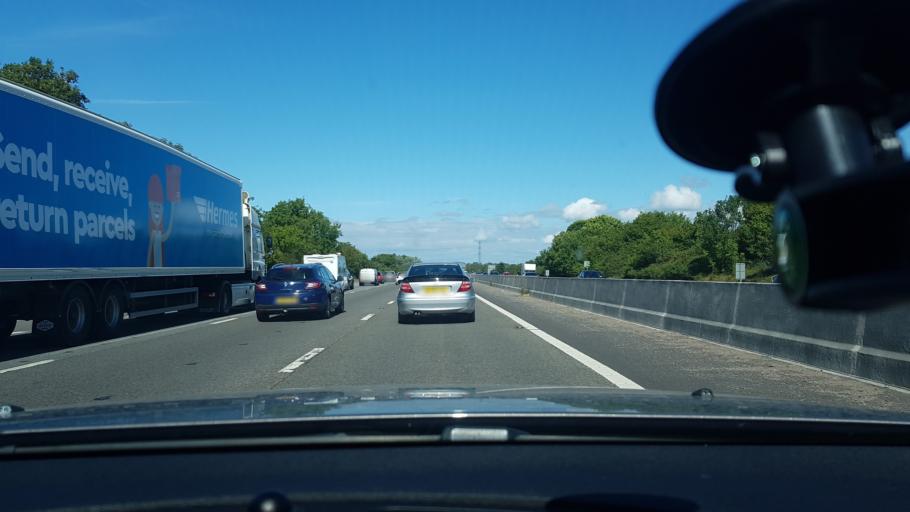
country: GB
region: England
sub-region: Somerset
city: Puriton
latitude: 51.1721
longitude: -2.9794
